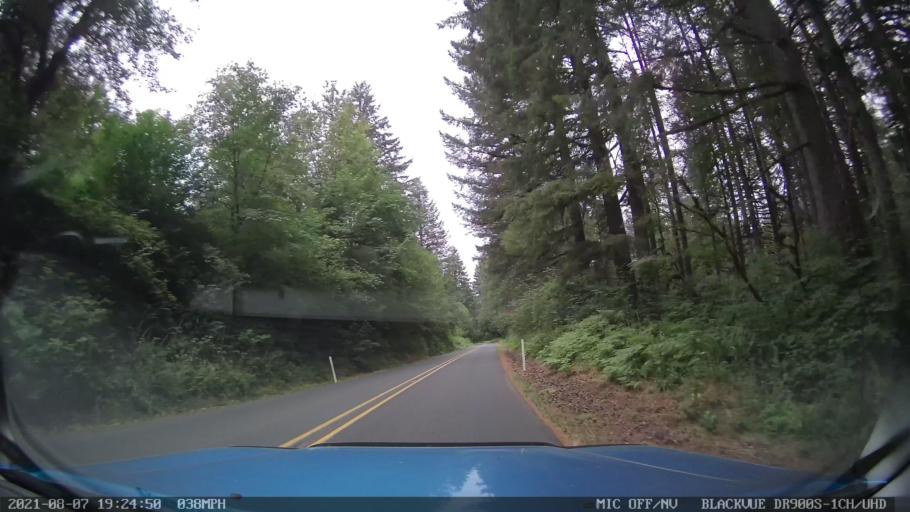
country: US
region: Oregon
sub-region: Linn County
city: Lyons
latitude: 44.8568
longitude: -122.6575
